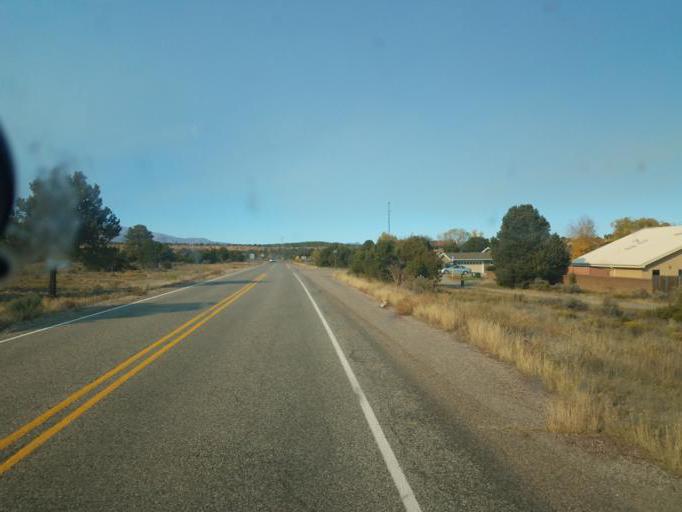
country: US
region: New Mexico
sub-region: Los Alamos County
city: White Rock
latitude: 35.8191
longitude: -106.2223
